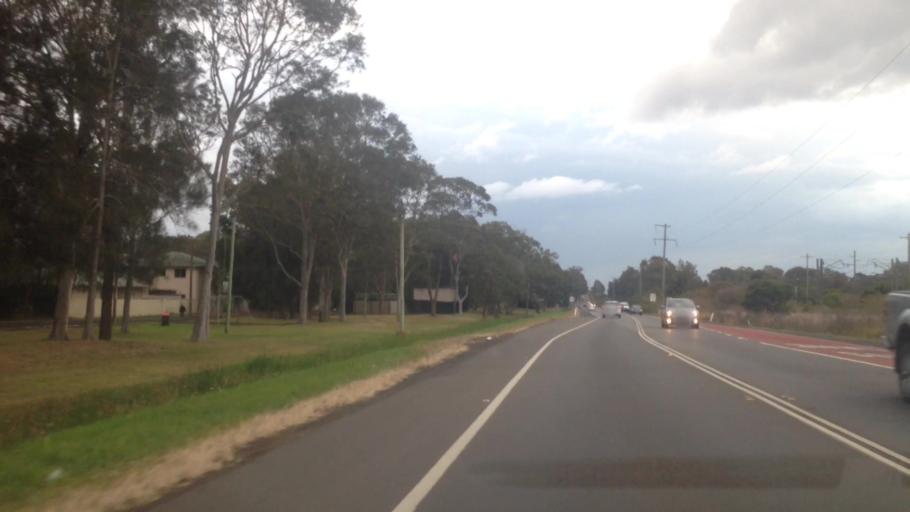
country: AU
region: New South Wales
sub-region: Wyong Shire
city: Chittaway Bay
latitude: -33.2796
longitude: 151.4271
